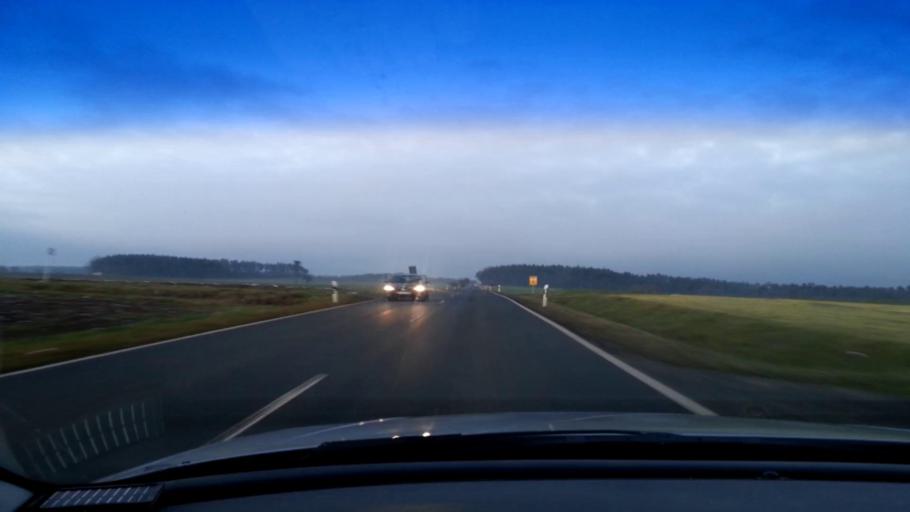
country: DE
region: Bavaria
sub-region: Upper Franconia
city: Pommersfelden
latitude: 49.7884
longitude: 10.8252
